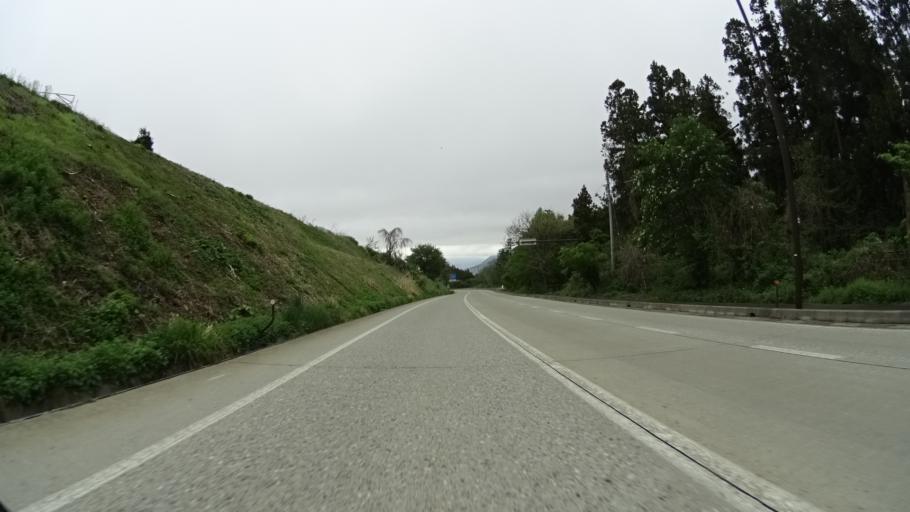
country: JP
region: Nagano
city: Nakano
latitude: 36.7320
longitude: 138.4210
